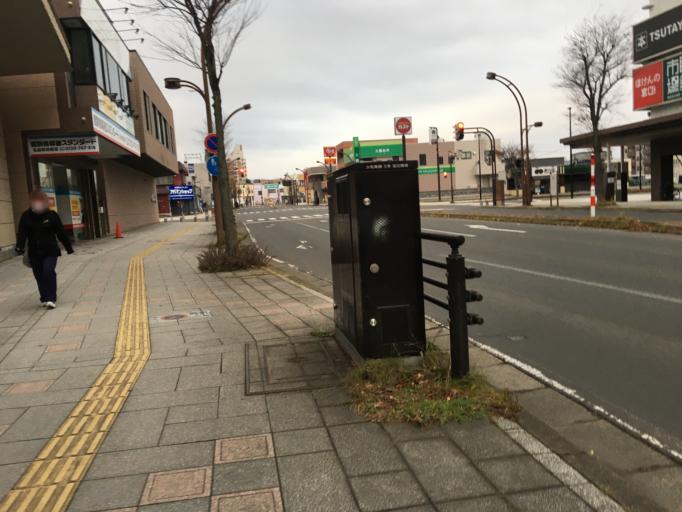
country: JP
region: Aomori
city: Hirosaki
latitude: 40.5969
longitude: 140.4822
